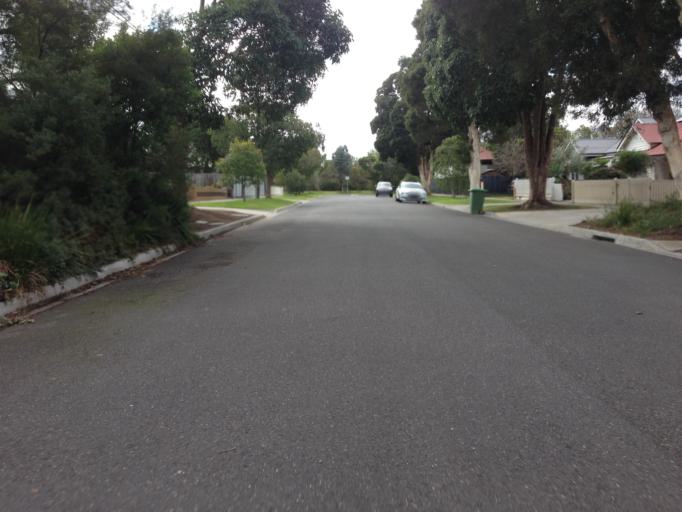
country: AU
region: Victoria
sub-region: Darebin
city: Fairfield
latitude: -37.7803
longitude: 145.0134
